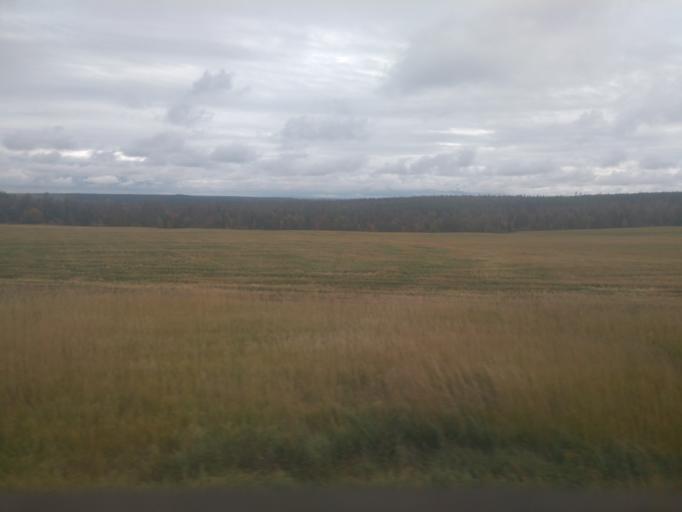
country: RU
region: Udmurtiya
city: Alnashi
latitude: 56.1431
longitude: 52.5725
